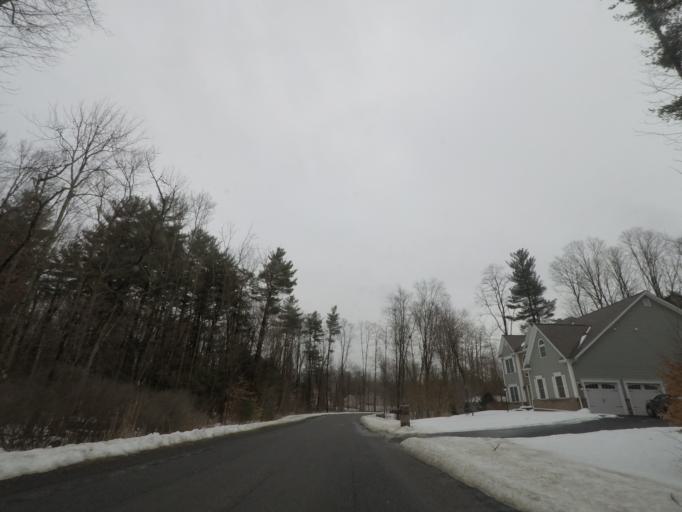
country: US
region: New York
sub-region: Schenectady County
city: Rotterdam
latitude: 42.7584
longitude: -73.9655
